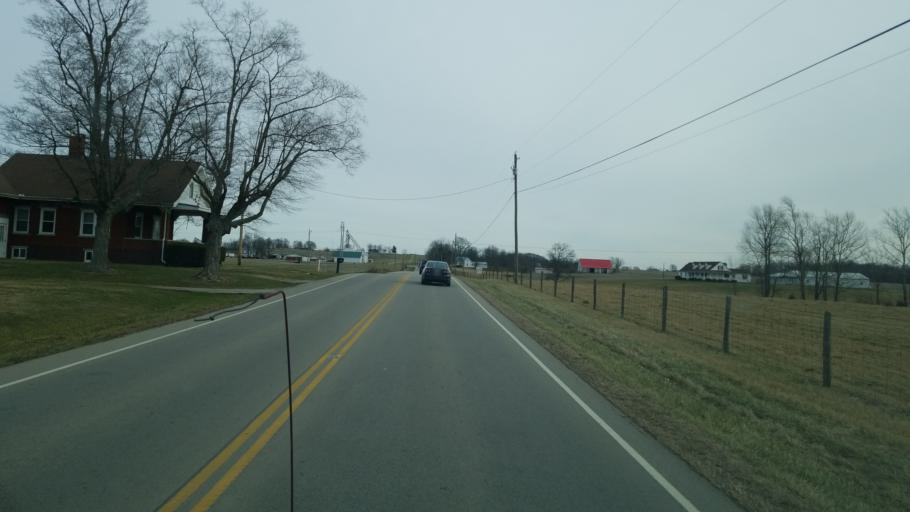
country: US
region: Ohio
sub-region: Adams County
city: Winchester
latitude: 39.0649
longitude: -83.6964
